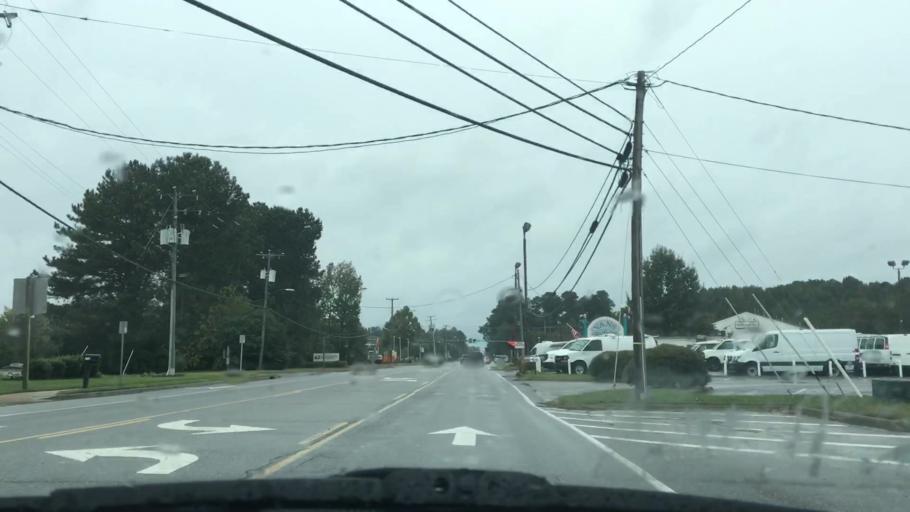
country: US
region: Virginia
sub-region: City of Chesapeake
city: Chesapeake
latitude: 36.6869
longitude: -76.2300
